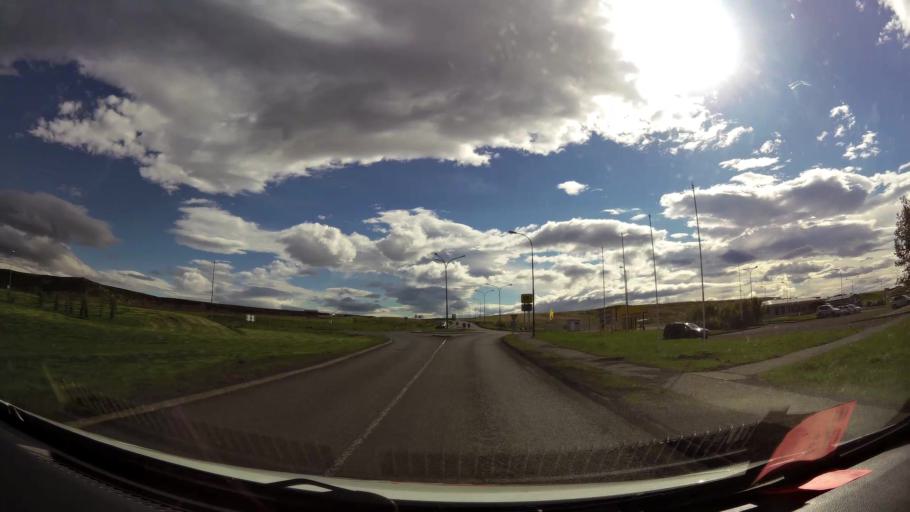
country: IS
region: Northwest
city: Saudarkrokur
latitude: 65.6566
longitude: -20.2836
